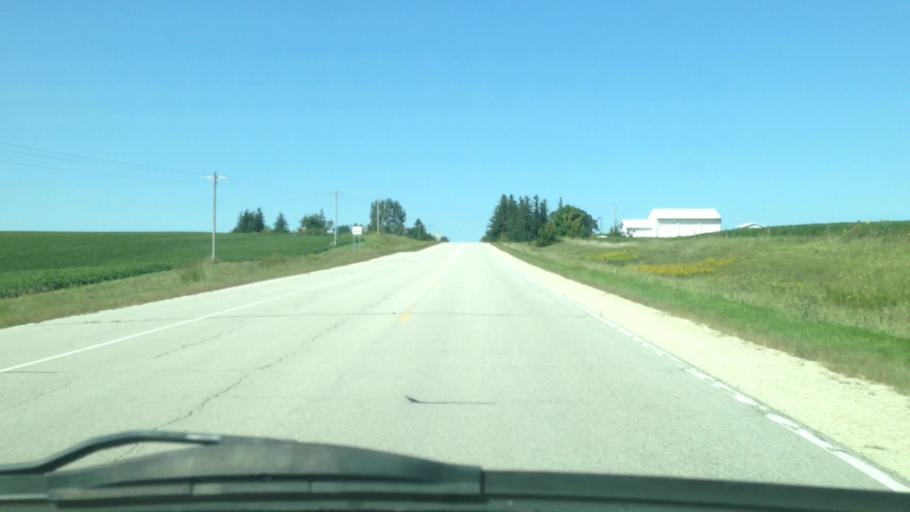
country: US
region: Minnesota
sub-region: Houston County
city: Spring Grove
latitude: 43.6167
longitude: -91.7904
